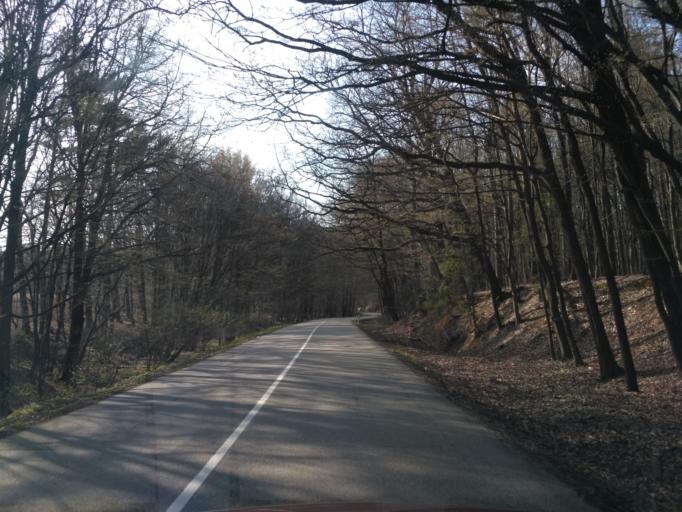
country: SK
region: Kosicky
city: Kosice
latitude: 48.6747
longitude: 21.1463
